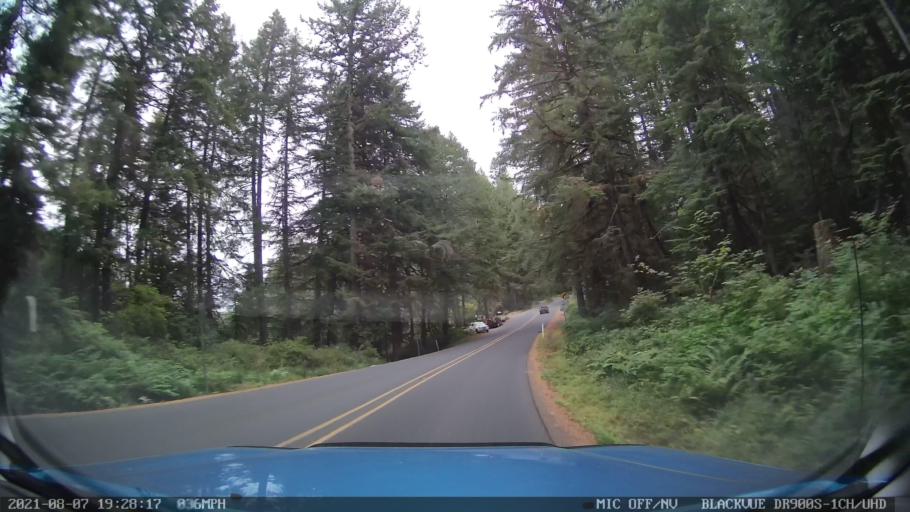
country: US
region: Oregon
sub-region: Linn County
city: Lyons
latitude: 44.8838
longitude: -122.6409
